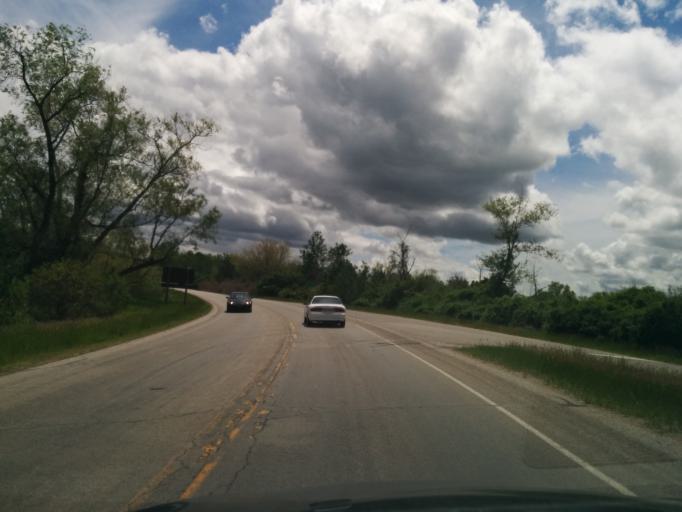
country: US
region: Indiana
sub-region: LaPorte County
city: Michigan City
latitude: 41.7044
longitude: -86.9324
